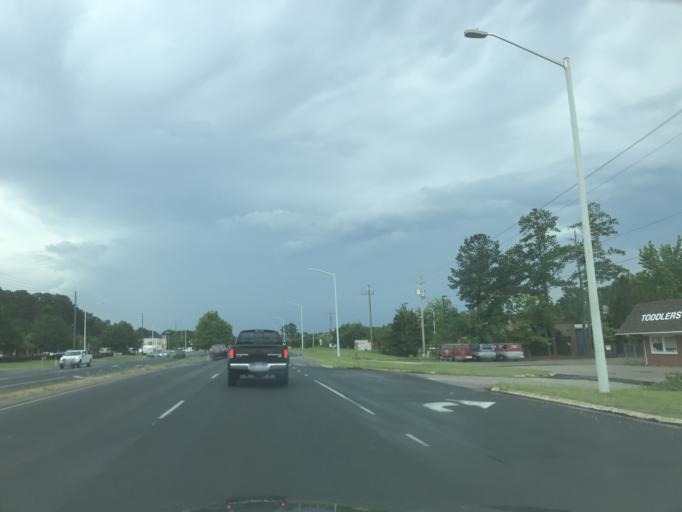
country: US
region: North Carolina
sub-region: Johnston County
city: Clayton
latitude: 35.6534
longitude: -78.4731
